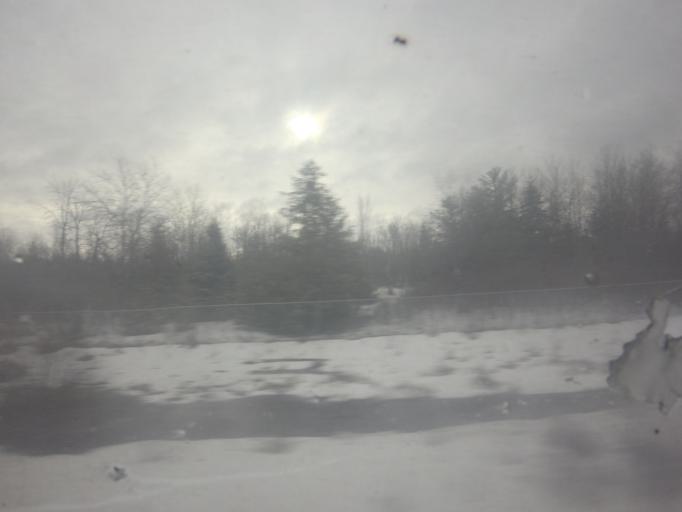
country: CA
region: Ontario
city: Bells Corners
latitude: 45.1213
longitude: -75.8681
